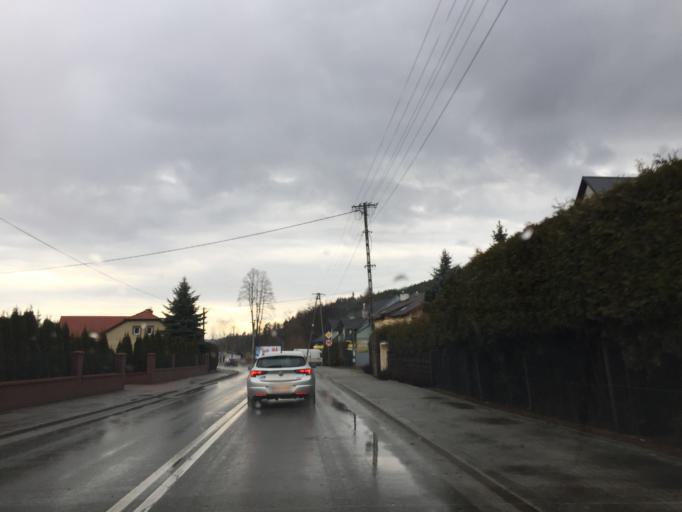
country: PL
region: Lesser Poland Voivodeship
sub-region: Powiat myslenicki
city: Sulkowice
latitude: 49.8532
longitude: 19.8000
